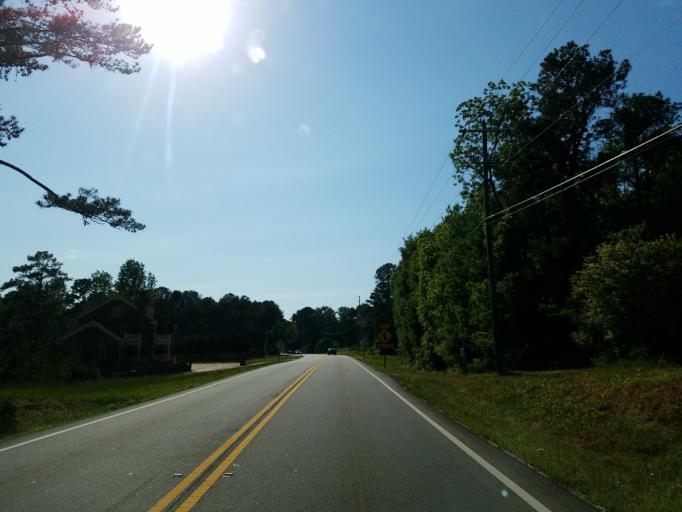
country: US
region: Georgia
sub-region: Paulding County
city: Hiram
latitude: 33.9184
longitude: -84.7830
